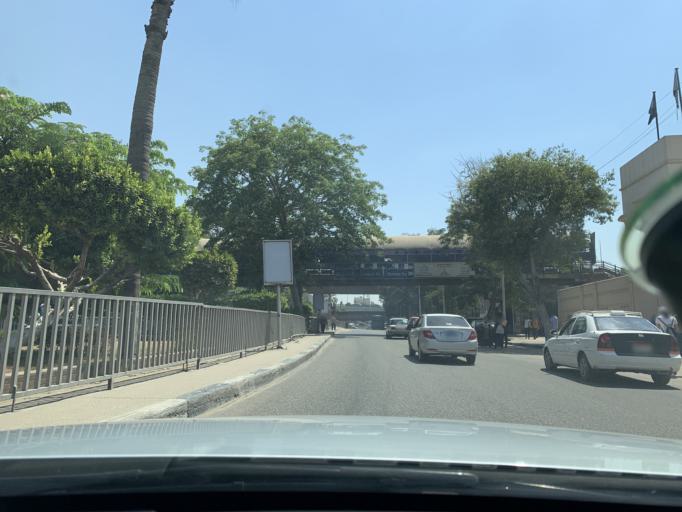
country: EG
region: Muhafazat al Qahirah
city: Cairo
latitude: 30.0757
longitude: 31.2869
